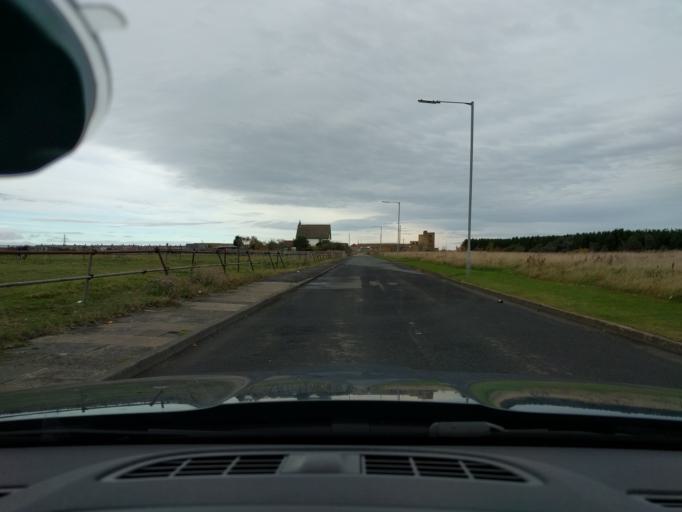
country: GB
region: England
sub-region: Northumberland
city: Blyth
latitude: 55.1523
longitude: -1.5243
